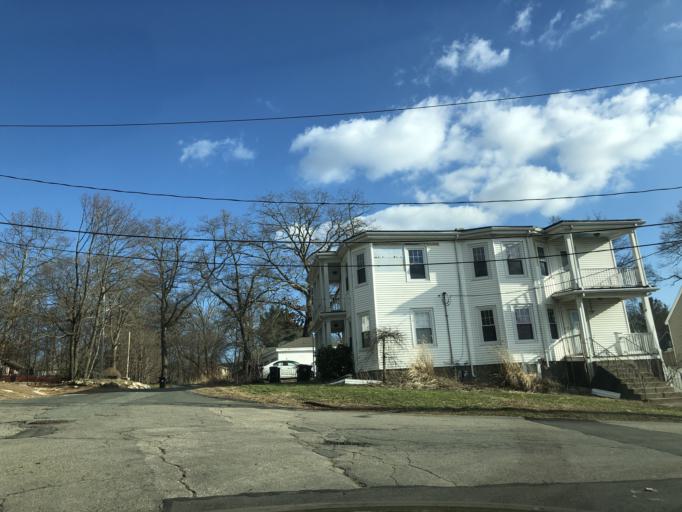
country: US
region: Massachusetts
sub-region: Plymouth County
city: Brockton
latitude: 42.1028
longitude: -71.0094
